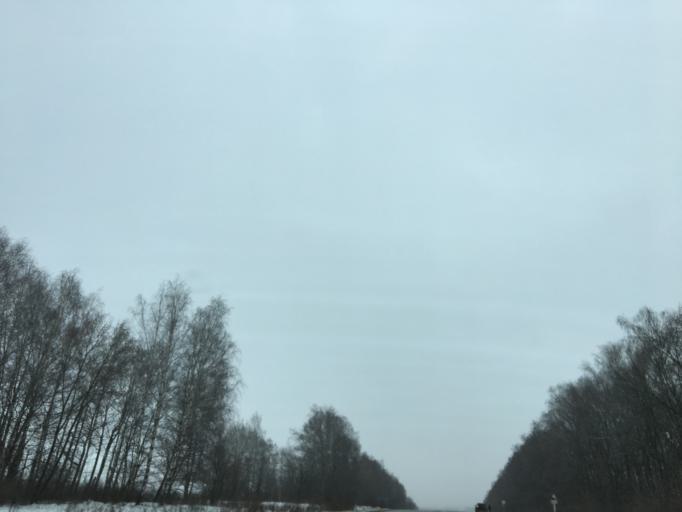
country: RU
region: Tula
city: Bolokhovo
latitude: 54.0420
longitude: 37.8631
